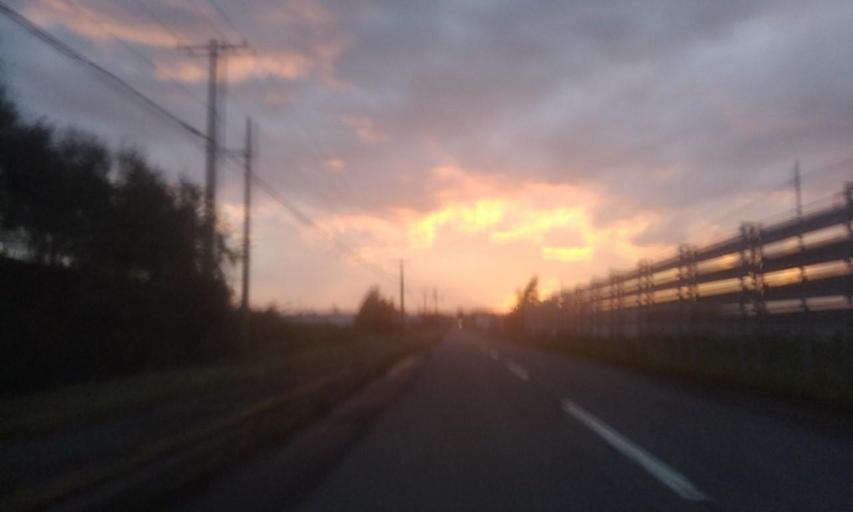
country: JP
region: Hokkaido
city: Abashiri
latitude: 43.8932
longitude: 144.4910
